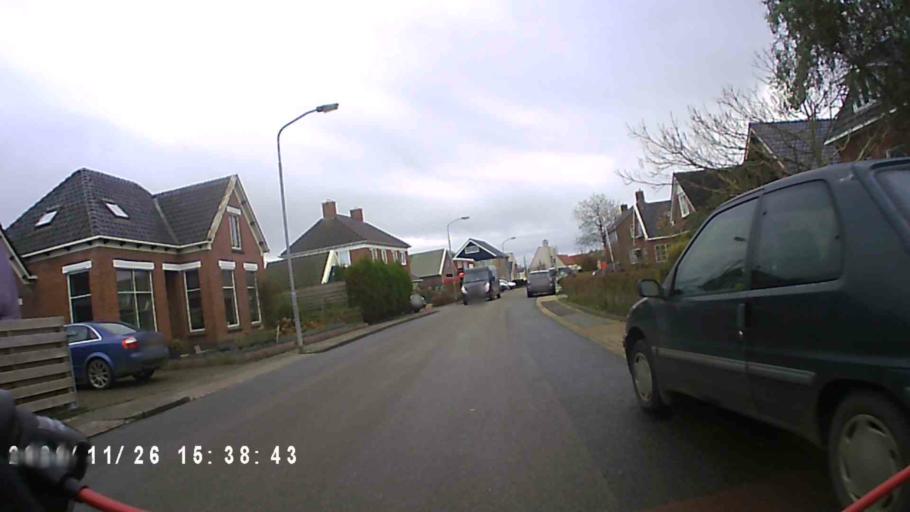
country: NL
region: Groningen
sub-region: Gemeente Slochteren
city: Slochteren
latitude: 53.2979
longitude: 6.7296
